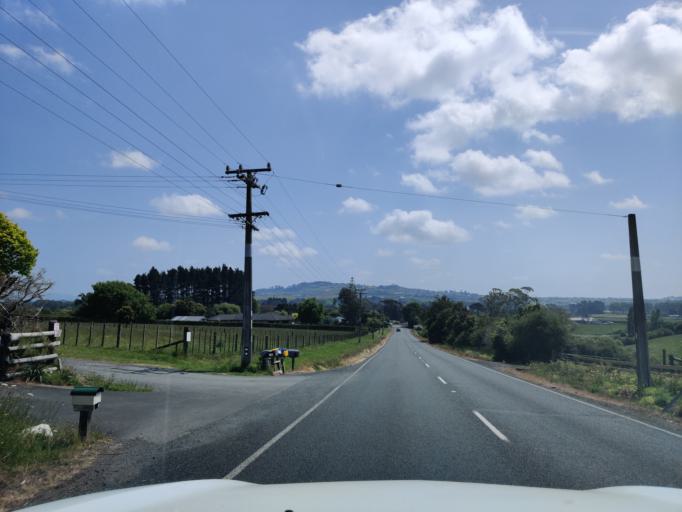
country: NZ
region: Auckland
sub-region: Auckland
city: Pukekohe East
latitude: -37.2139
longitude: 174.9404
